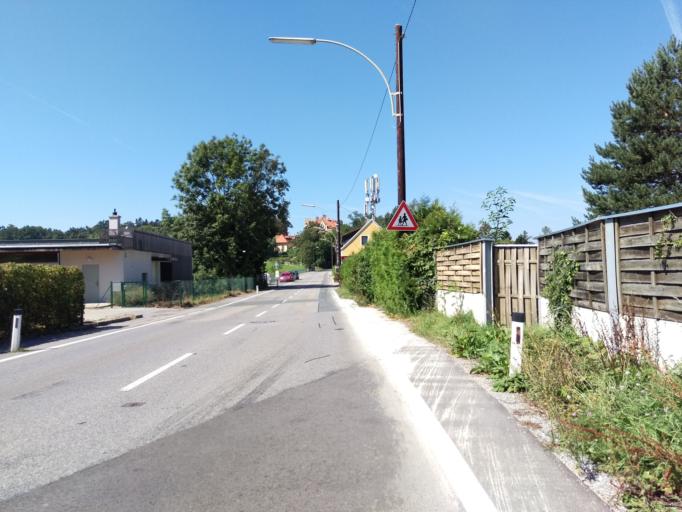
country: AT
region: Styria
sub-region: Graz Stadt
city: Mariatrost
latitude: 47.0697
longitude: 15.5001
